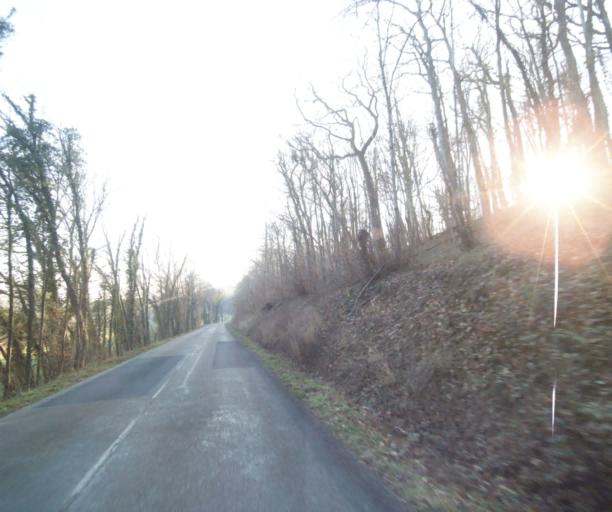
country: FR
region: Champagne-Ardenne
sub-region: Departement de la Haute-Marne
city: Bienville
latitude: 48.5685
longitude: 5.0791
